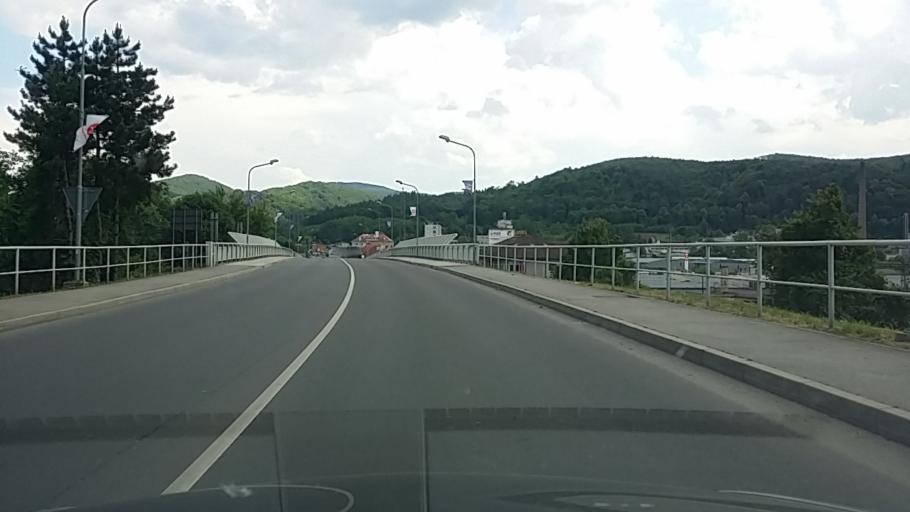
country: SK
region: Banskobystricky
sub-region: Okres Banska Bystrica
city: Zvolen
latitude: 48.5724
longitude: 19.1264
